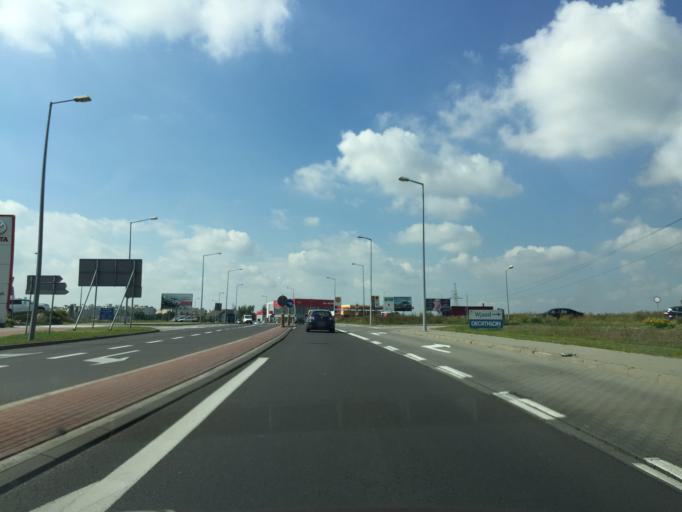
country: PL
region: Greater Poland Voivodeship
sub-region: Kalisz
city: Kalisz
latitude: 51.7633
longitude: 18.0612
